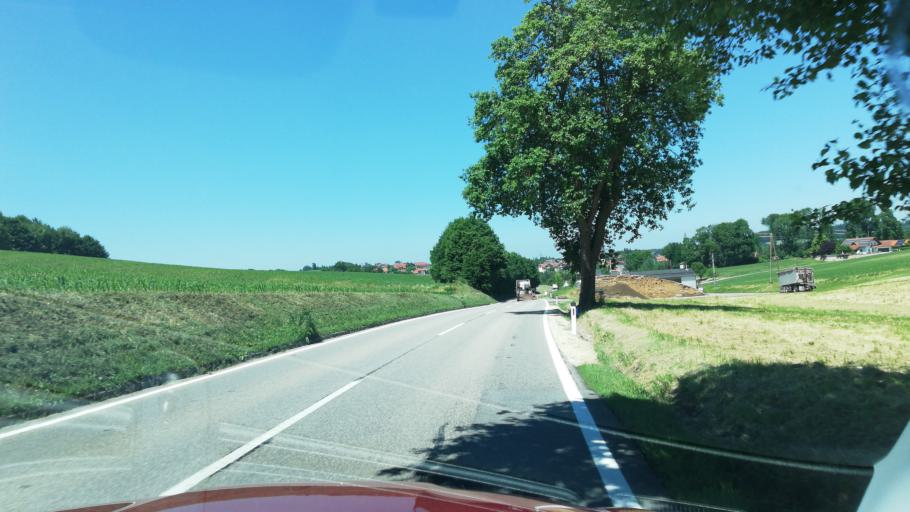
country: AT
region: Upper Austria
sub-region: Politischer Bezirk Vocklabruck
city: Niederthalheim
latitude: 48.1333
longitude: 13.7365
